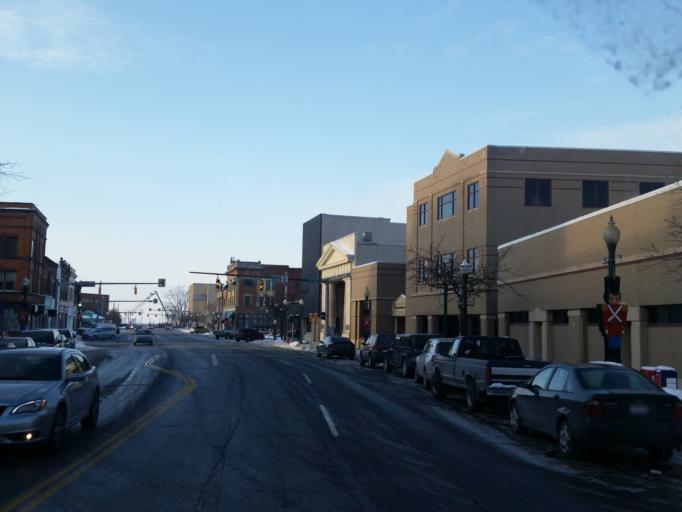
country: US
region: Ohio
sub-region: Lorain County
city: Lorain
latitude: 41.4663
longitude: -82.1757
